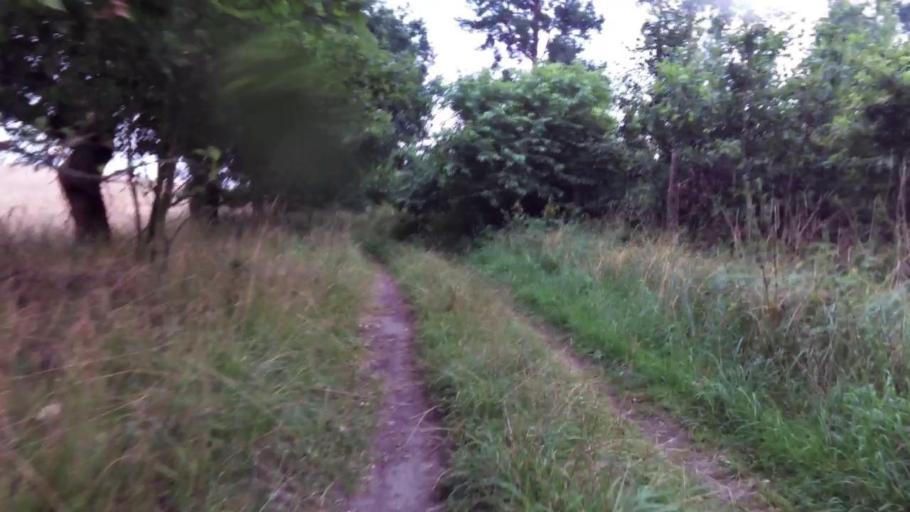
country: PL
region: West Pomeranian Voivodeship
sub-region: Powiat drawski
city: Drawsko Pomorskie
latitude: 53.5396
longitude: 15.7108
